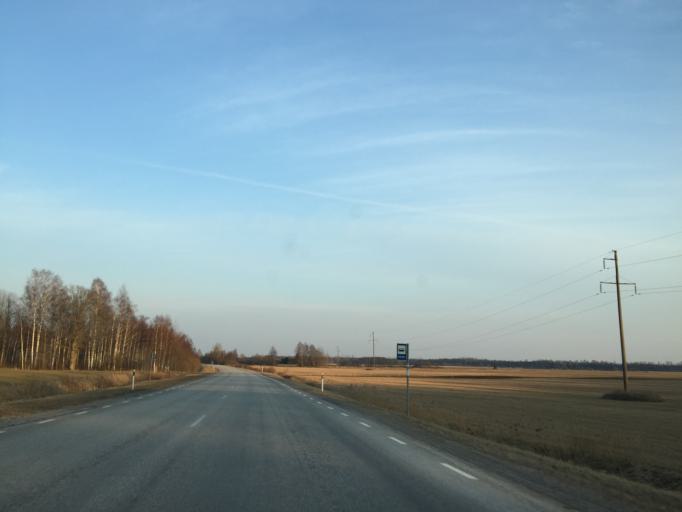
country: EE
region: Laeaene
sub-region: Lihula vald
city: Lihula
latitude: 58.5386
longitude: 24.0143
